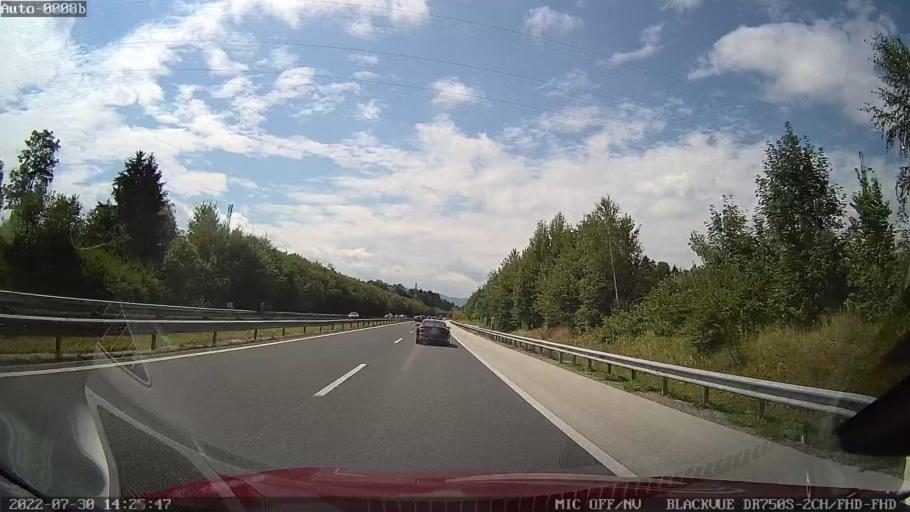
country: SI
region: Kranj
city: Kokrica
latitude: 46.2628
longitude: 14.3547
